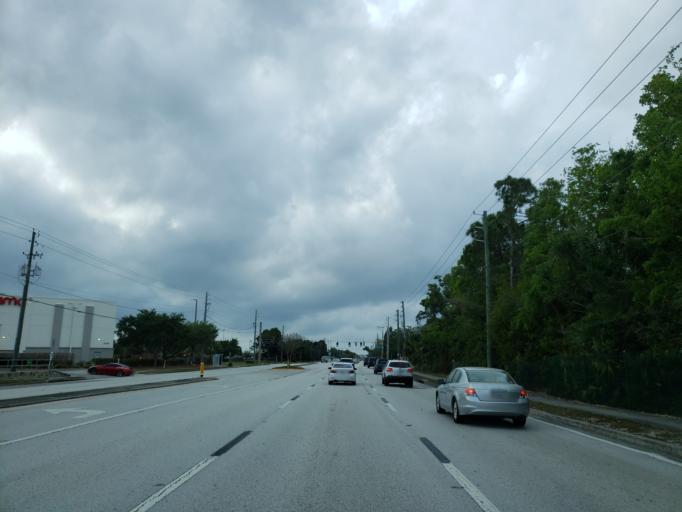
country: US
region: Florida
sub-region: Pinellas County
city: Saint George
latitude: 28.0522
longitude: -82.6986
